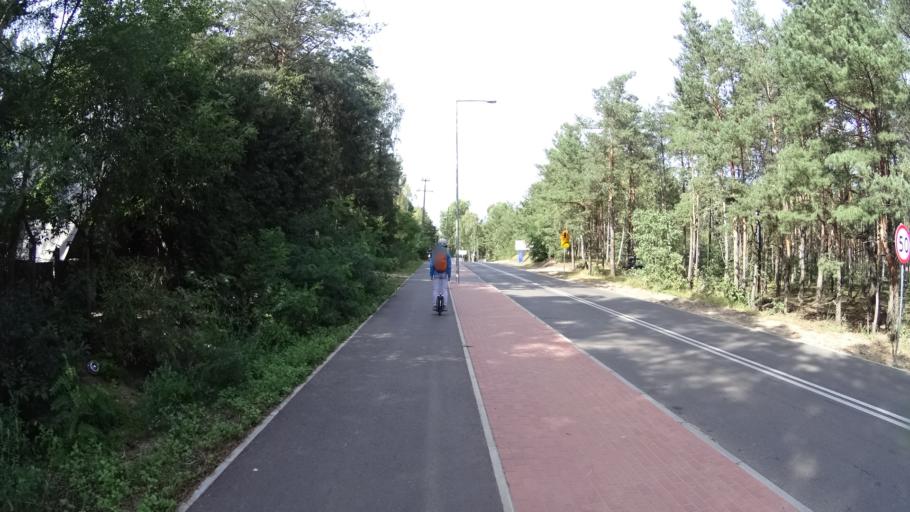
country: PL
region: Masovian Voivodeship
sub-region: Powiat legionowski
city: Bialobrzegi
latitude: 52.4633
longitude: 21.0764
